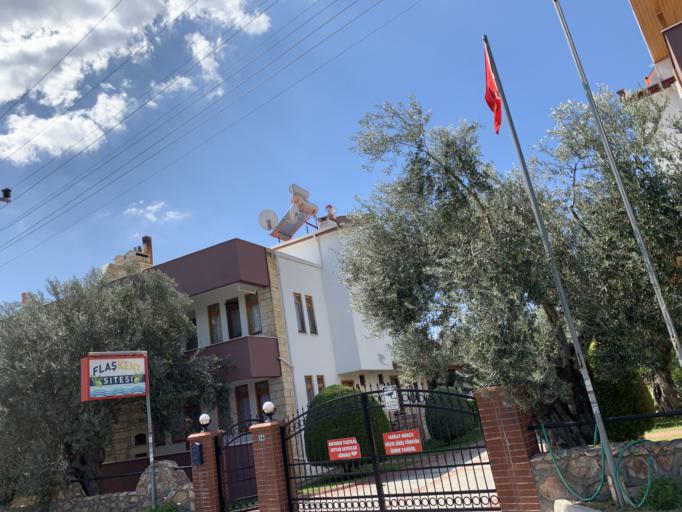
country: TR
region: Balikesir
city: Altinoluk
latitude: 39.5678
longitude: 26.8354
